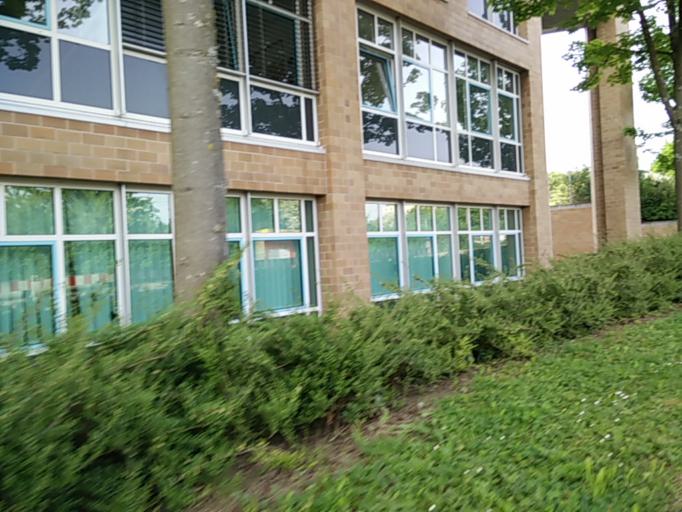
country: DE
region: Baden-Wuerttemberg
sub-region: Regierungsbezirk Stuttgart
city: Boeblingen
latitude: 48.6847
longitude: 9.0009
